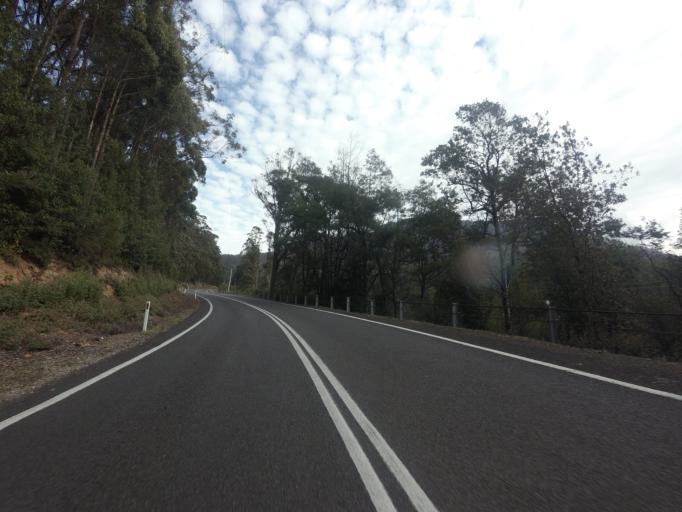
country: AU
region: Tasmania
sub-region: Meander Valley
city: Deloraine
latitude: -41.6467
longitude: 146.7209
